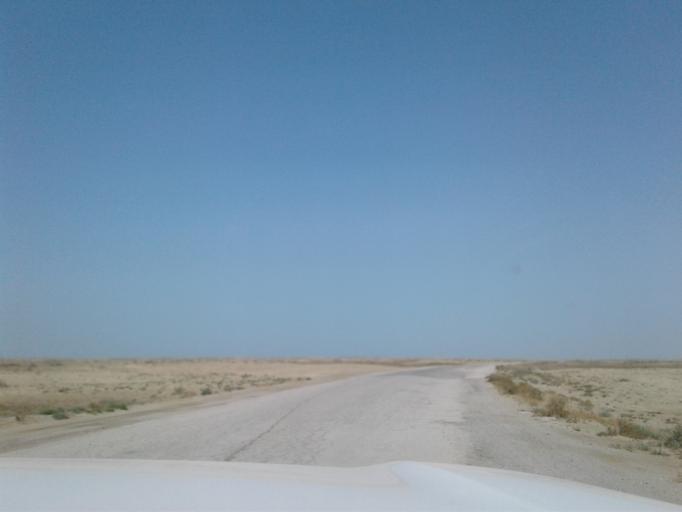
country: IR
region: Golestan
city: Gomishan
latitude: 37.9131
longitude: 53.8518
